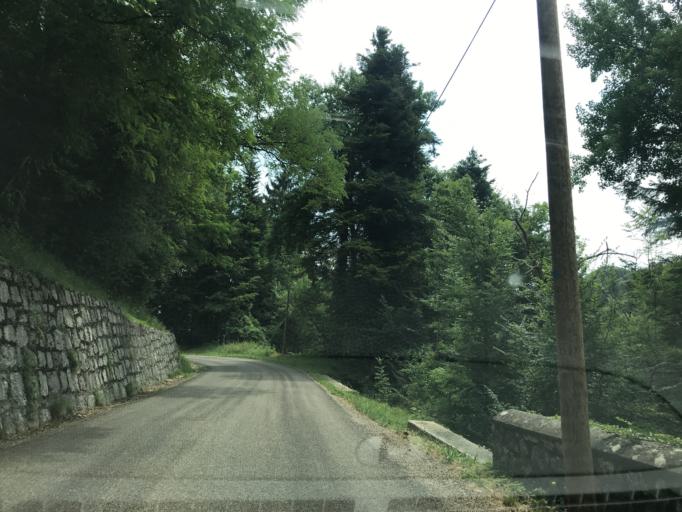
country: FR
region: Rhone-Alpes
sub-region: Departement de l'Isere
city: Barraux
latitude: 45.4571
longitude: 5.9575
